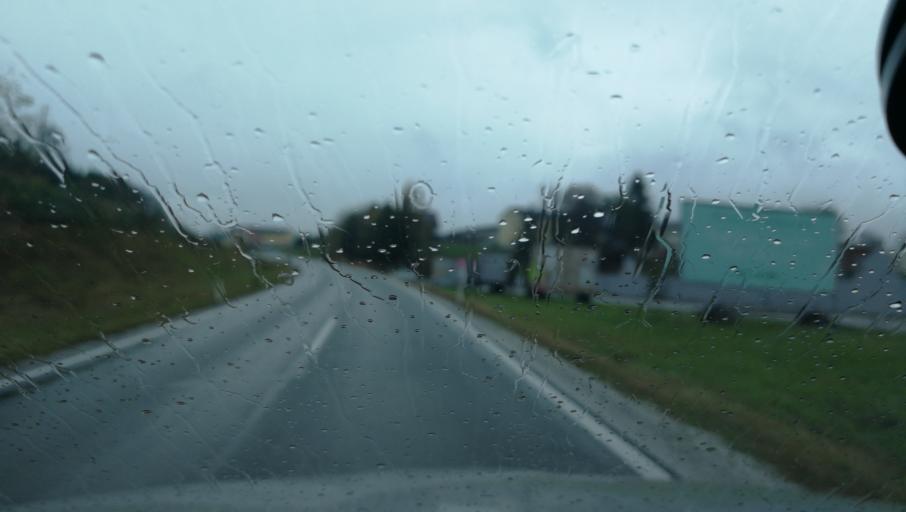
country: AT
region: Styria
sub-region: Politischer Bezirk Leibnitz
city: Sankt Veit am Vogau
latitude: 46.7488
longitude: 15.6229
